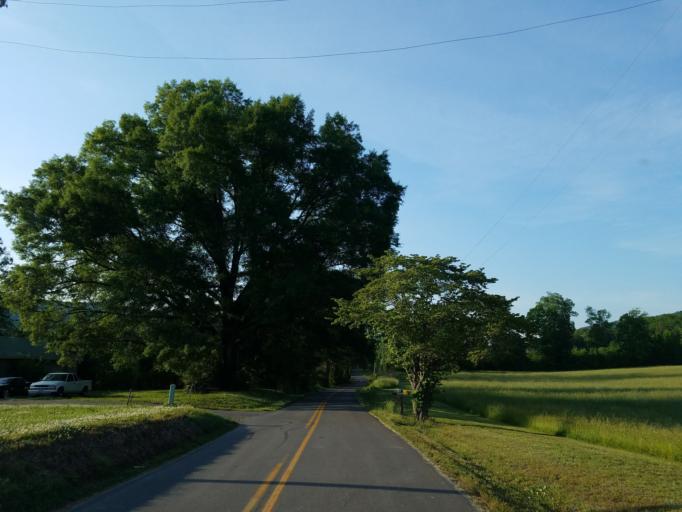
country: US
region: Georgia
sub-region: Gordon County
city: Calhoun
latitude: 34.5389
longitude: -85.1076
